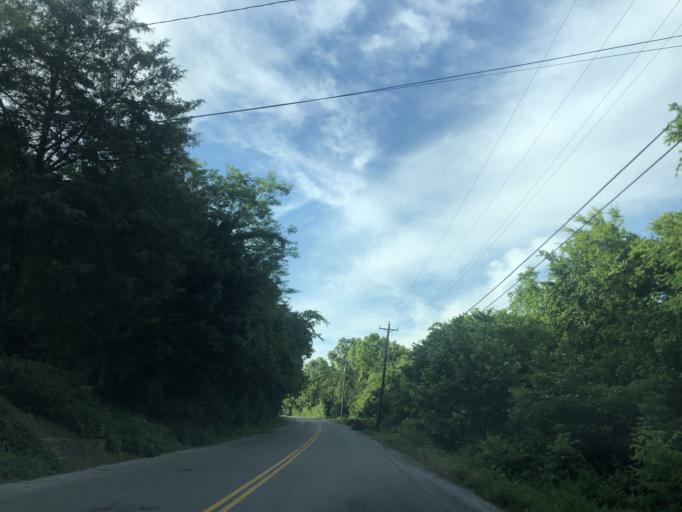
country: US
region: Tennessee
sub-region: Davidson County
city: Nashville
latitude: 36.2140
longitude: -86.8481
